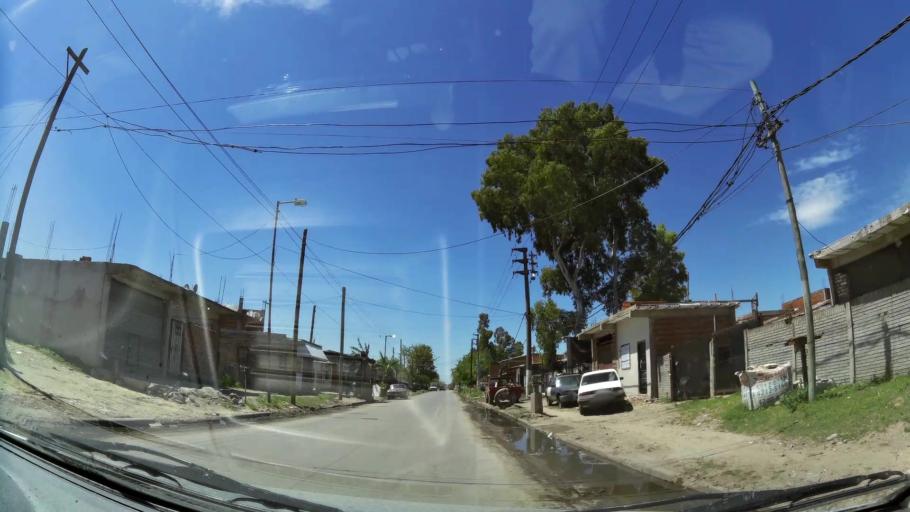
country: AR
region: Buenos Aires
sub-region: Partido de Quilmes
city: Quilmes
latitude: -34.7283
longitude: -58.3190
